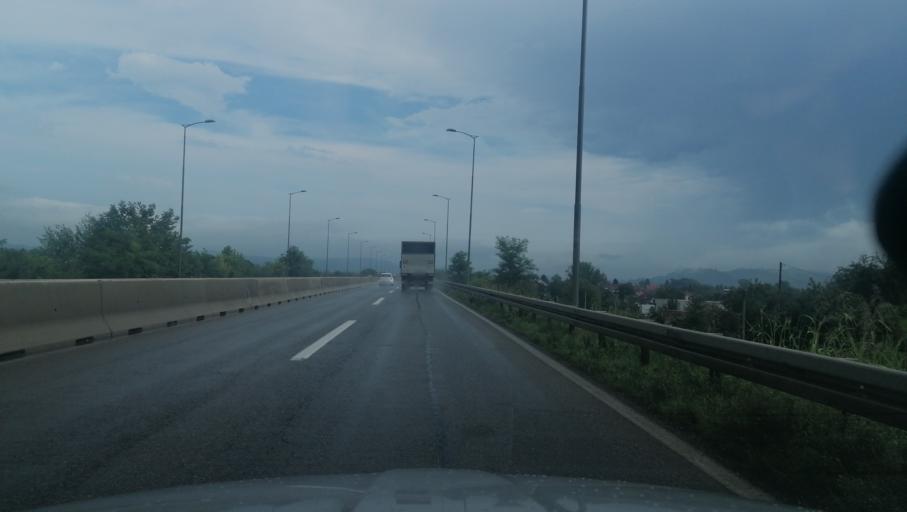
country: BA
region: Republika Srpska
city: Trn
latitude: 44.8358
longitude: 17.2163
